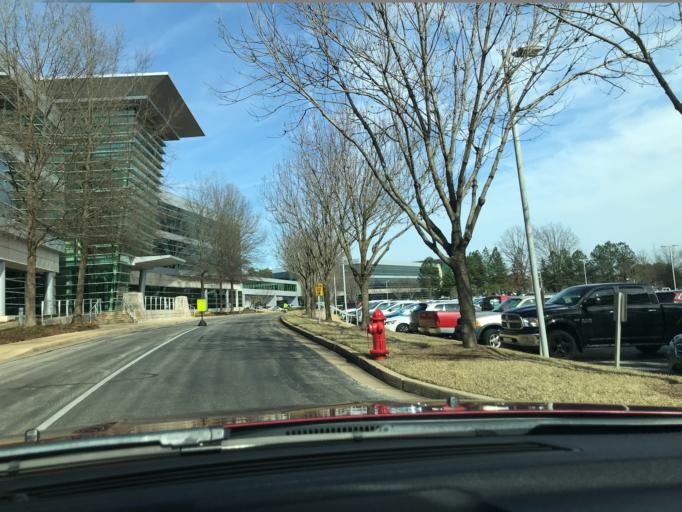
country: US
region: Tennessee
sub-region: Shelby County
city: Germantown
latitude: 35.0494
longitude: -89.7886
